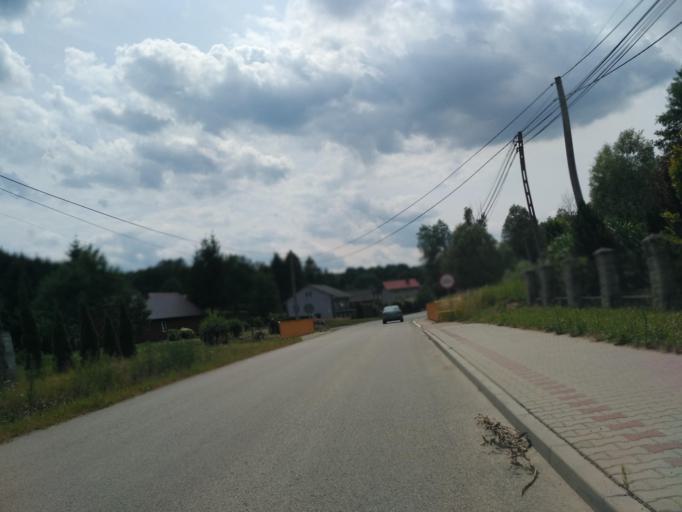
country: PL
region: Subcarpathian Voivodeship
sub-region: Powiat ropczycko-sedziszowski
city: Niedzwiada
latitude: 50.0389
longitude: 21.4973
